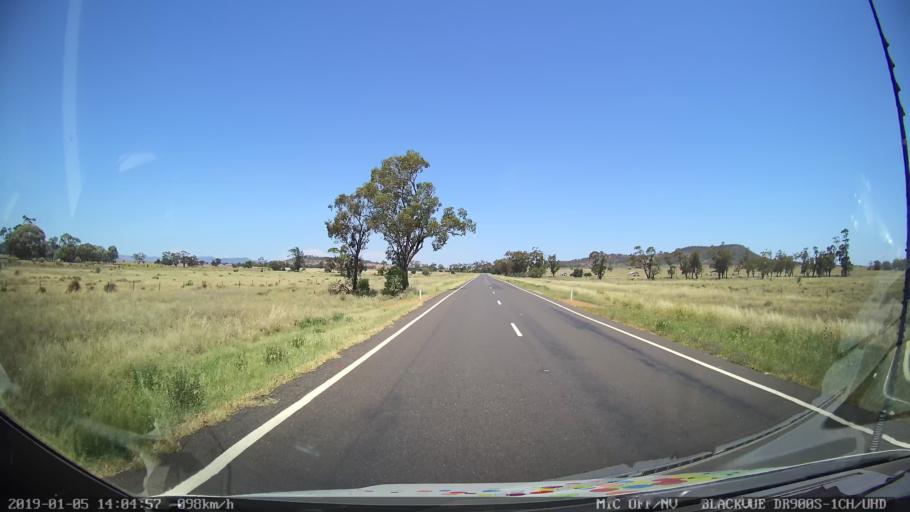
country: AU
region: New South Wales
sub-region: Gunnedah
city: Gunnedah
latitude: -31.2052
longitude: 150.3698
